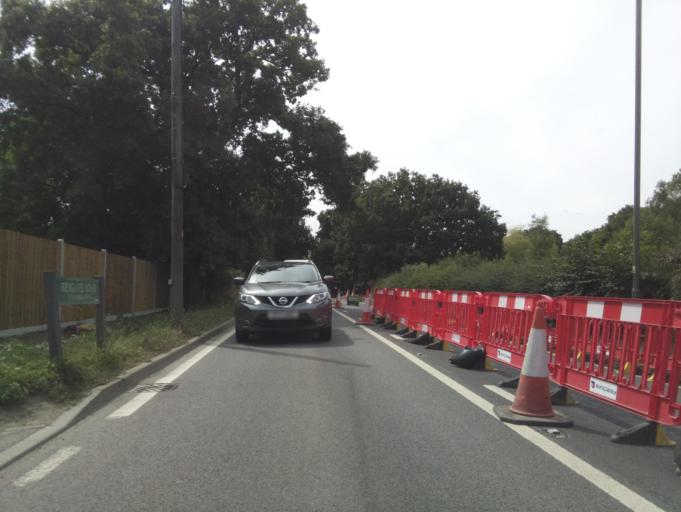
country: GB
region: England
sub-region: Surrey
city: Salfords
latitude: 51.1840
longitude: -0.1956
